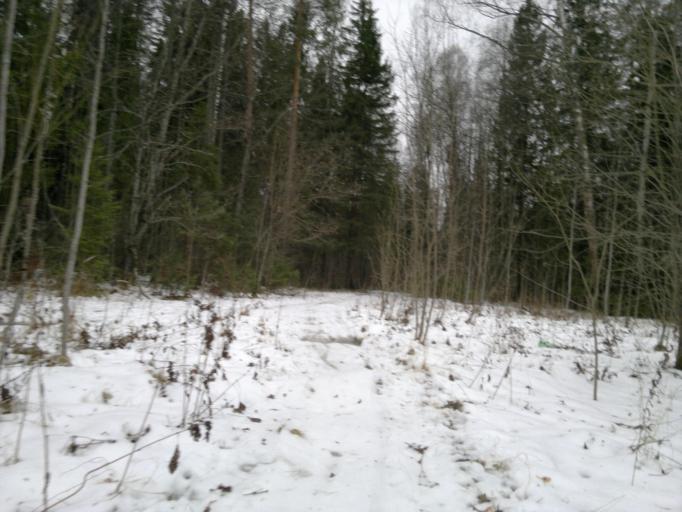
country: RU
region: Mariy-El
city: Yoshkar-Ola
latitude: 56.6053
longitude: 47.9621
